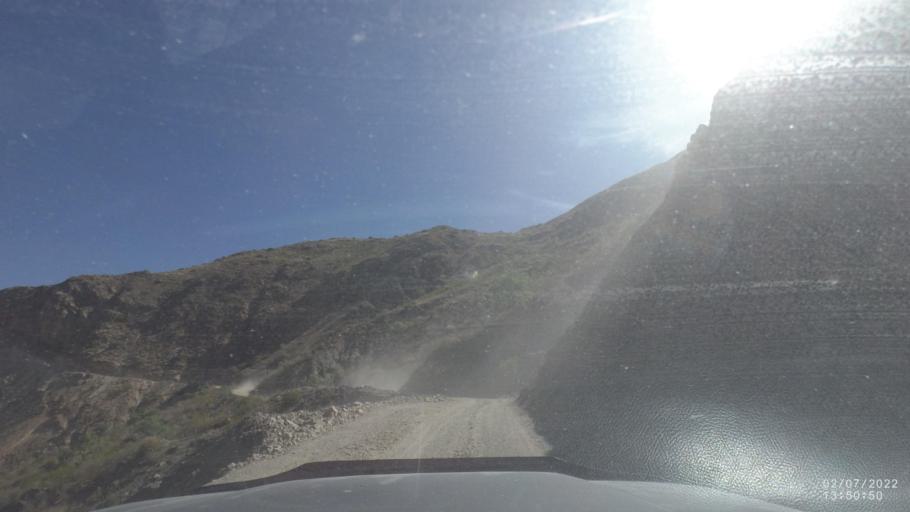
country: BO
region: Cochabamba
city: Irpa Irpa
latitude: -17.8219
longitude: -66.3794
